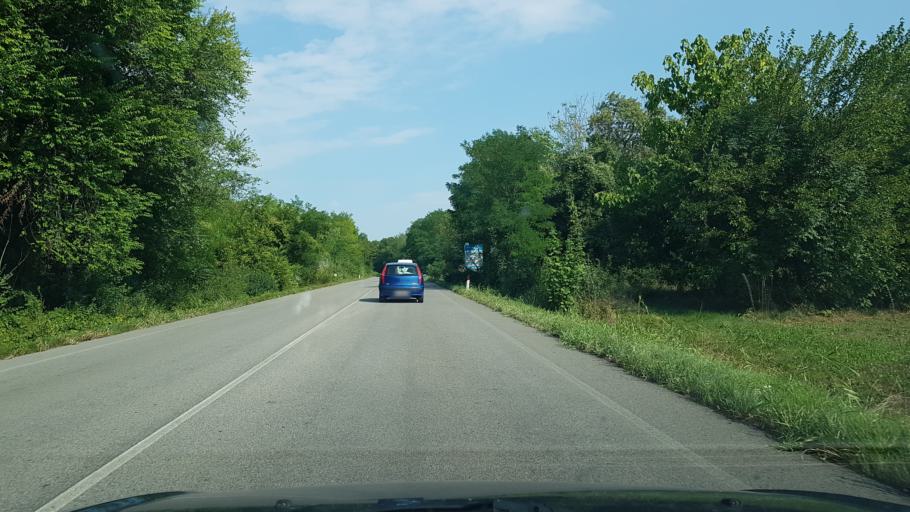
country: IT
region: Friuli Venezia Giulia
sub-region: Provincia di Udine
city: Colloredo di Prato
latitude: 46.0588
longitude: 13.1655
